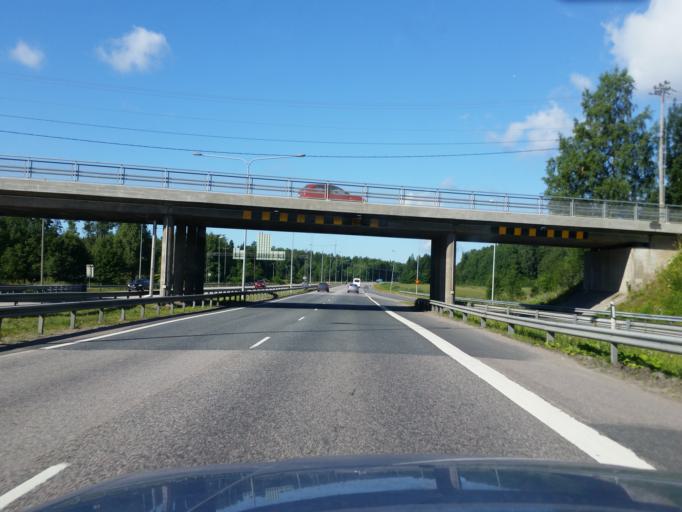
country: FI
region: Uusimaa
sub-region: Helsinki
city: Kauniainen
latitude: 60.2036
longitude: 24.7416
